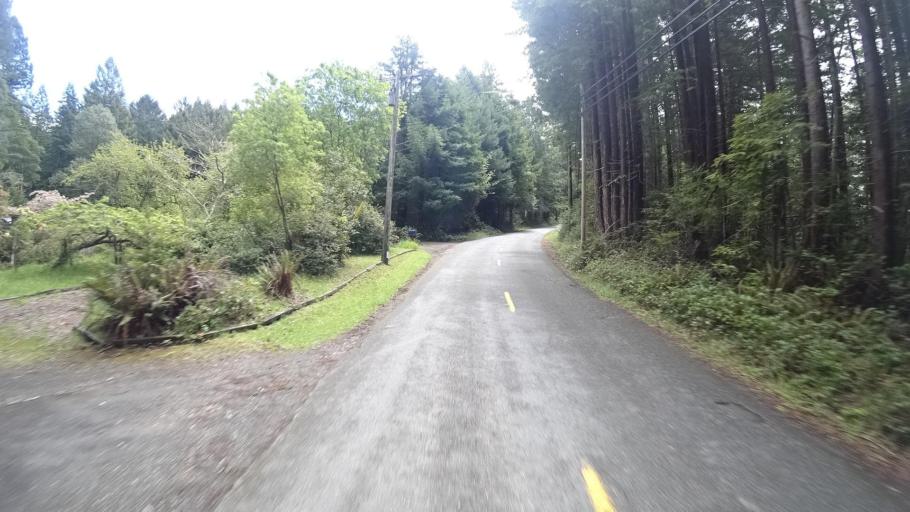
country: US
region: California
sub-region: Humboldt County
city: Bayside
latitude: 40.7816
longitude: -124.0088
